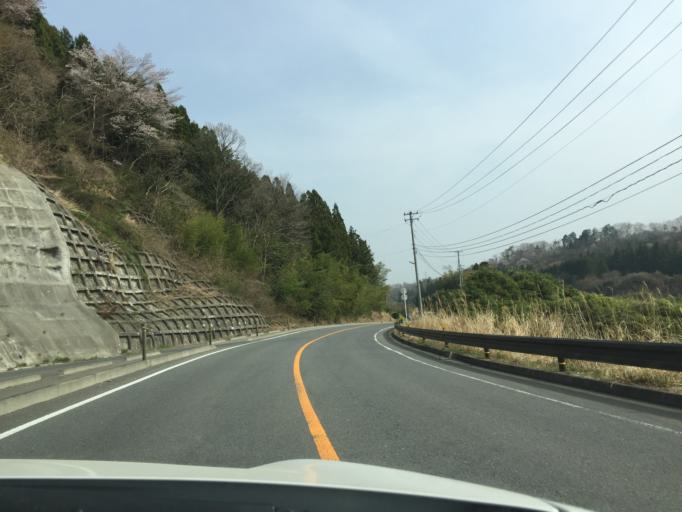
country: JP
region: Fukushima
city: Iwaki
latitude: 37.0137
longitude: 140.7731
